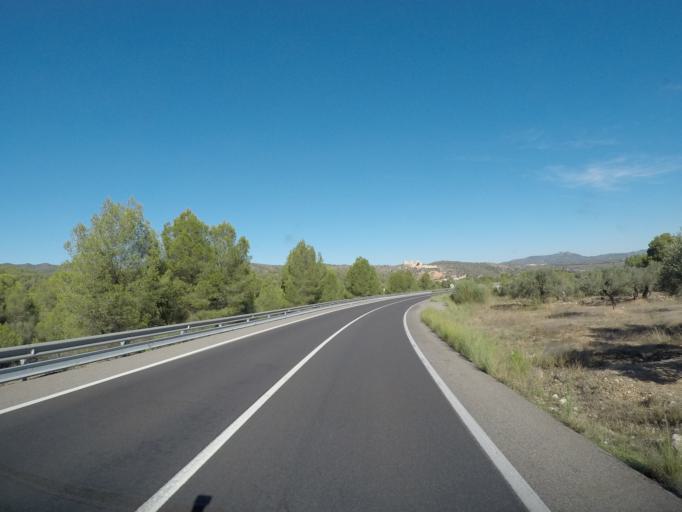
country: ES
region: Catalonia
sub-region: Provincia de Tarragona
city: Miravet
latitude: 41.0230
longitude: 0.6054
